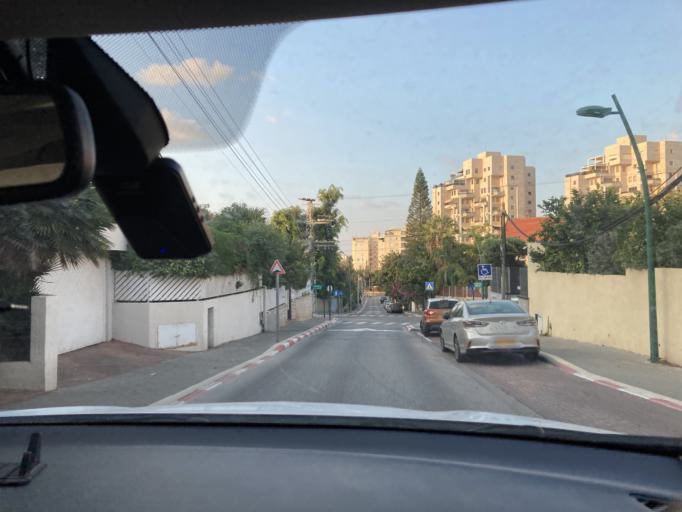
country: IL
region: Tel Aviv
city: Ramat HaSharon
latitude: 32.1505
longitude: 34.8396
